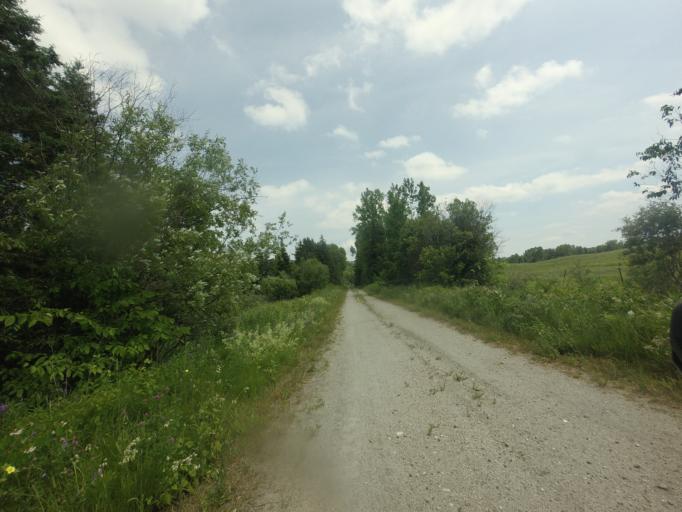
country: CA
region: Quebec
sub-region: Outaouais
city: Wakefield
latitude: 45.8233
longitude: -75.9774
